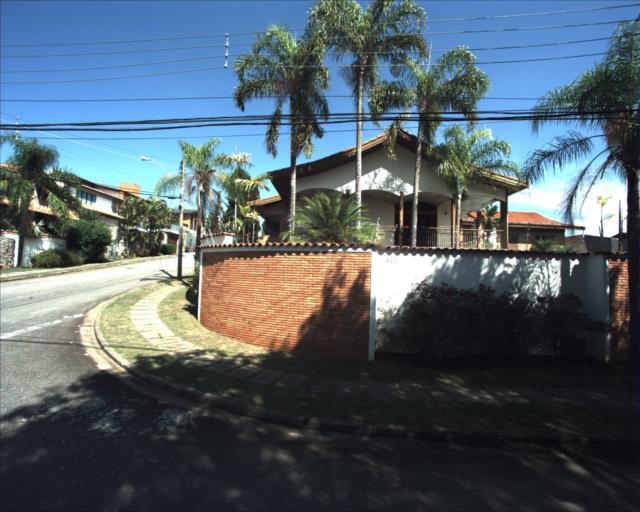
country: BR
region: Sao Paulo
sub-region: Sorocaba
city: Sorocaba
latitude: -23.5209
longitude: -47.4718
